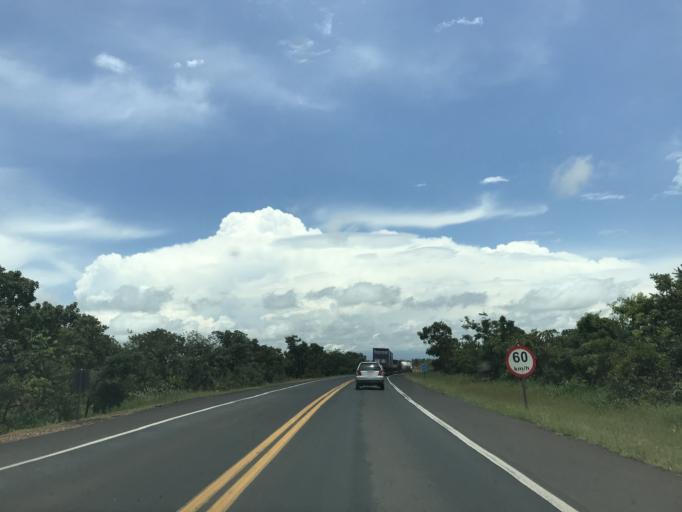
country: BR
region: Minas Gerais
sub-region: Frutal
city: Frutal
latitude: -19.6737
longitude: -48.9878
